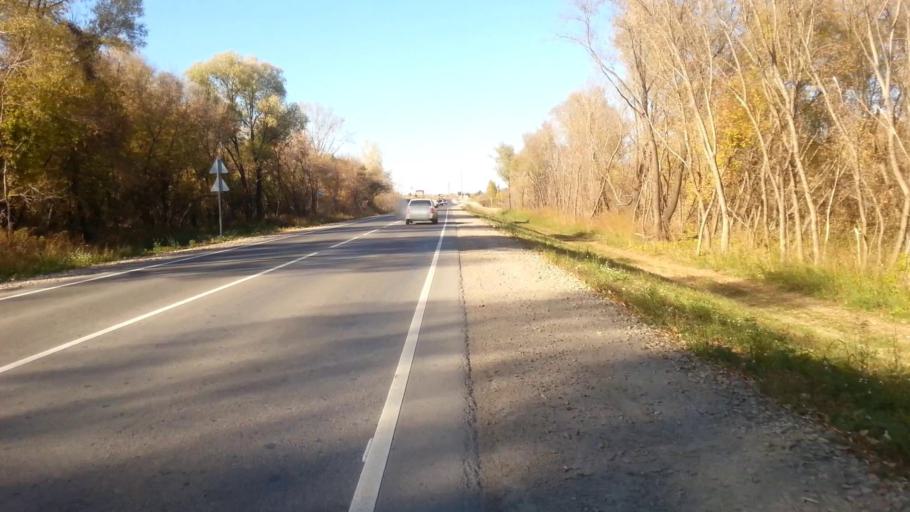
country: RU
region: Altai Krai
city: Sannikovo
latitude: 53.3242
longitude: 83.9427
